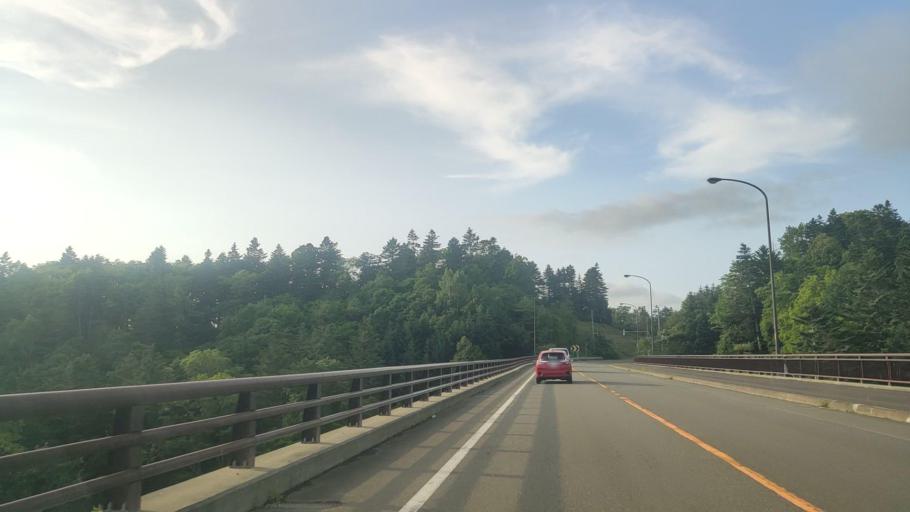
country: JP
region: Hokkaido
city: Iwamizawa
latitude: 43.0250
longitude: 141.9541
